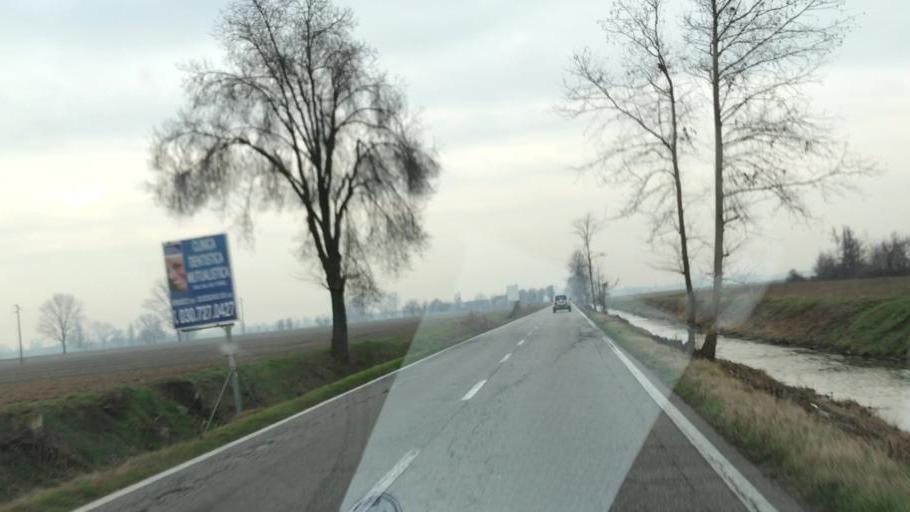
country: IT
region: Lombardy
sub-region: Provincia di Mantova
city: Casalmoro
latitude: 45.2450
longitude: 10.4157
